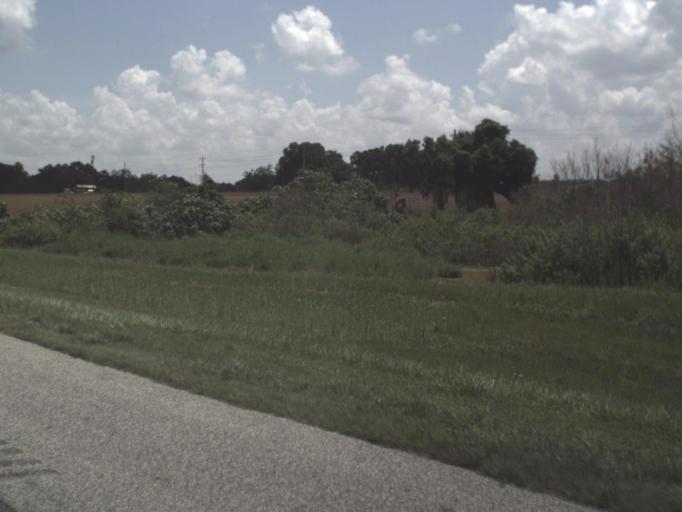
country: US
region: Florida
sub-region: Hillsborough County
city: Dover
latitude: 28.0269
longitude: -82.1958
